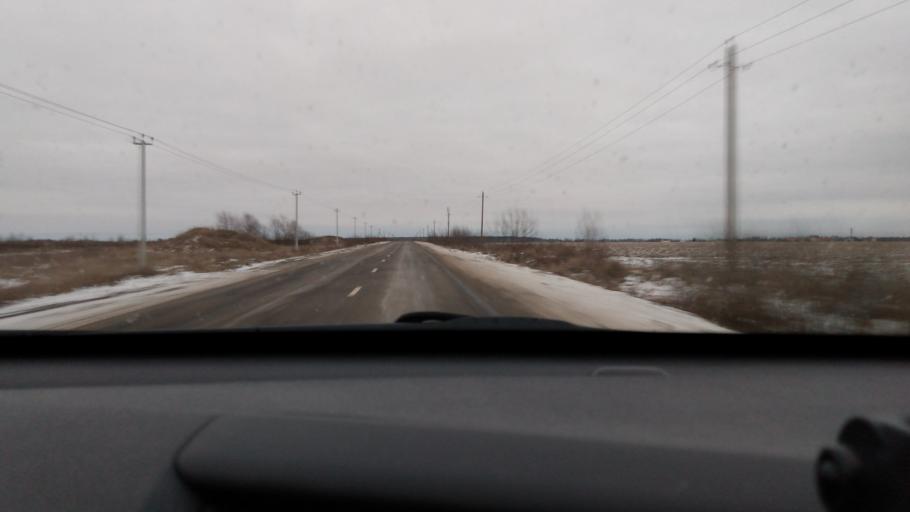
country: RU
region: Moskovskaya
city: Meshcherino
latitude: 55.2902
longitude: 38.3243
